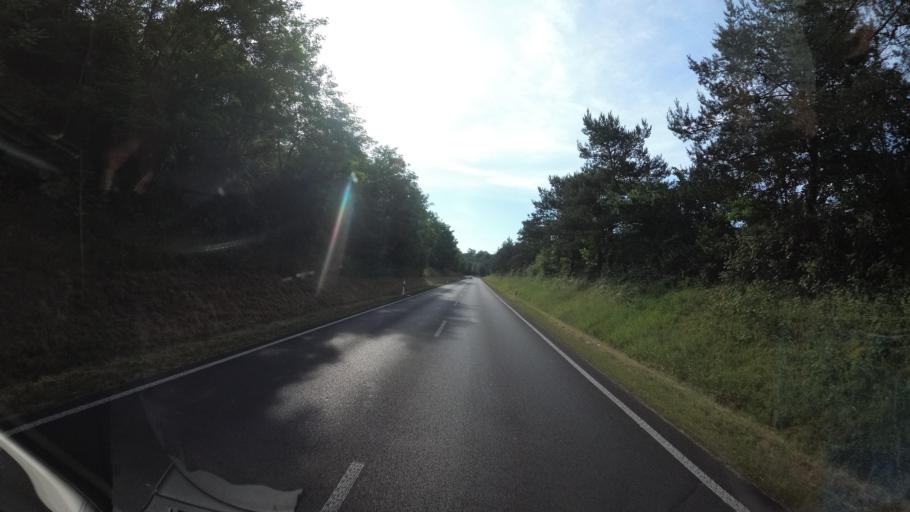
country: DE
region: Baden-Wuerttemberg
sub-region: Freiburg Region
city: Weil am Rhein
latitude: 47.5880
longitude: 7.6286
